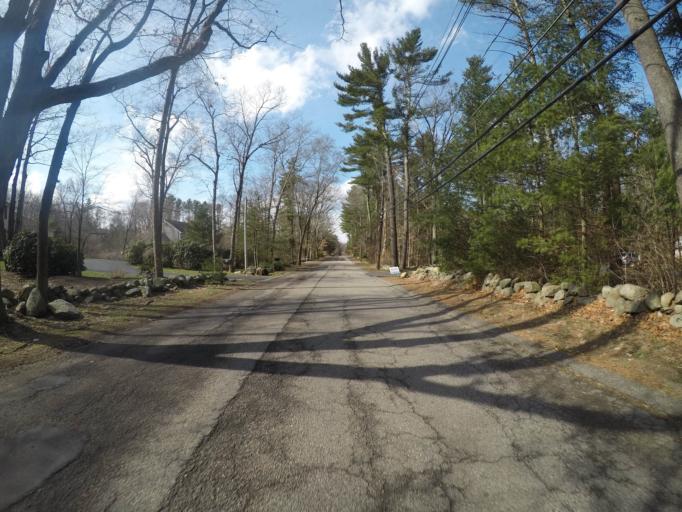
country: US
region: Massachusetts
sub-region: Bristol County
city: Easton
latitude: 42.0133
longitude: -71.1470
